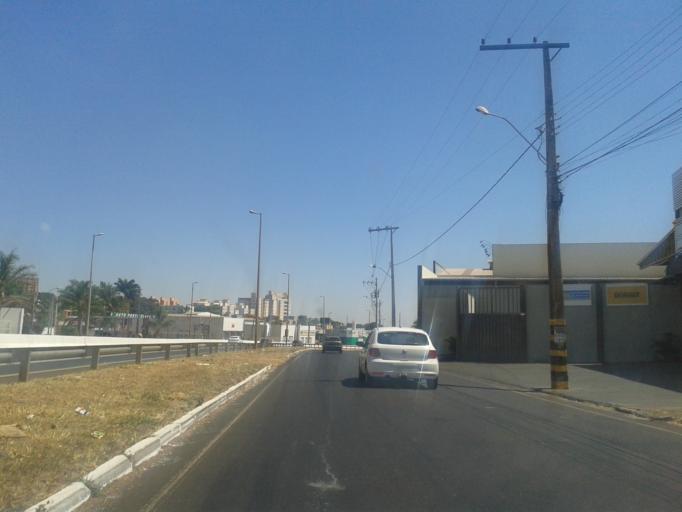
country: BR
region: Minas Gerais
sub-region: Uberlandia
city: Uberlandia
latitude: -18.9017
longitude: -48.2764
